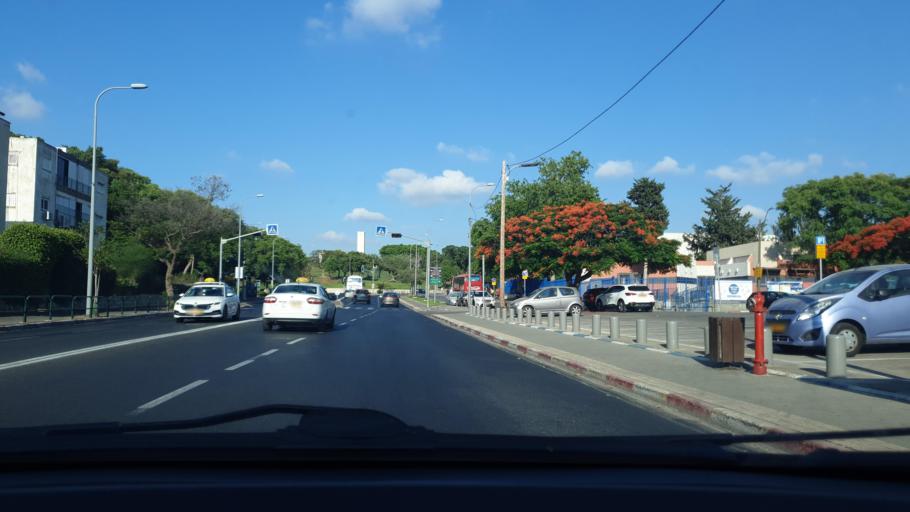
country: IL
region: Tel Aviv
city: Giv`atayim
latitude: 32.0592
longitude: 34.8019
